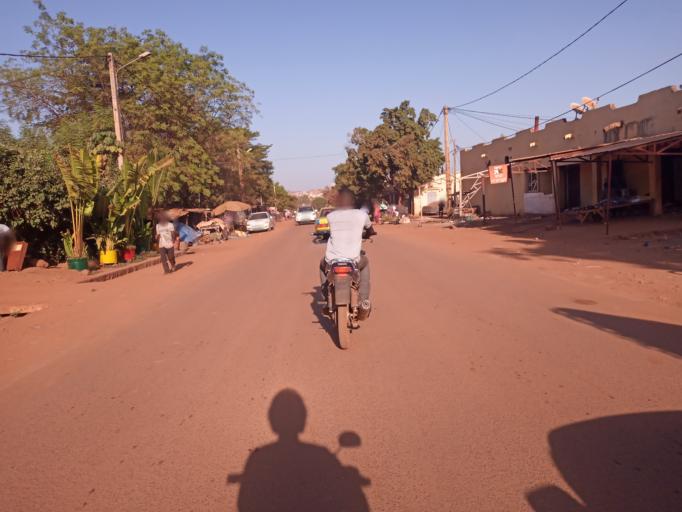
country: ML
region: Bamako
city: Bamako
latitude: 12.6123
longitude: -7.9537
